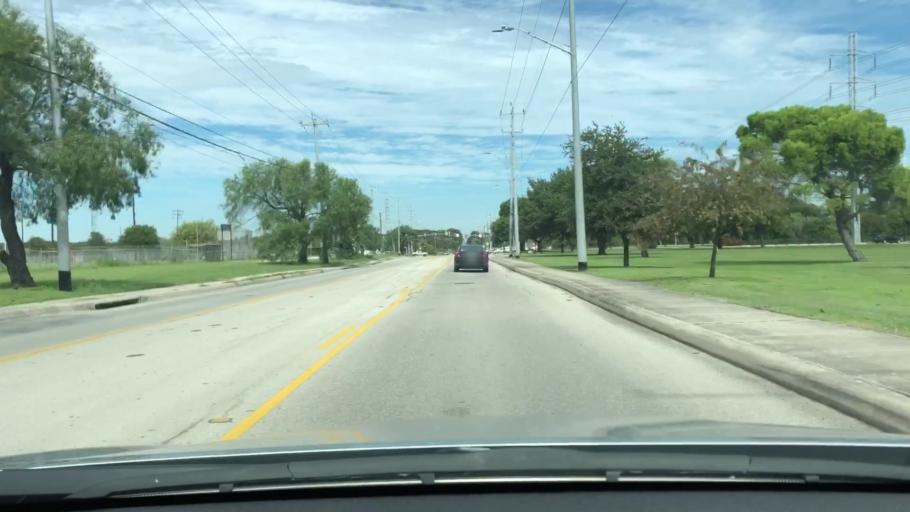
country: US
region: Texas
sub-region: Bexar County
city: Olmos Park
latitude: 29.4859
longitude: -98.4917
